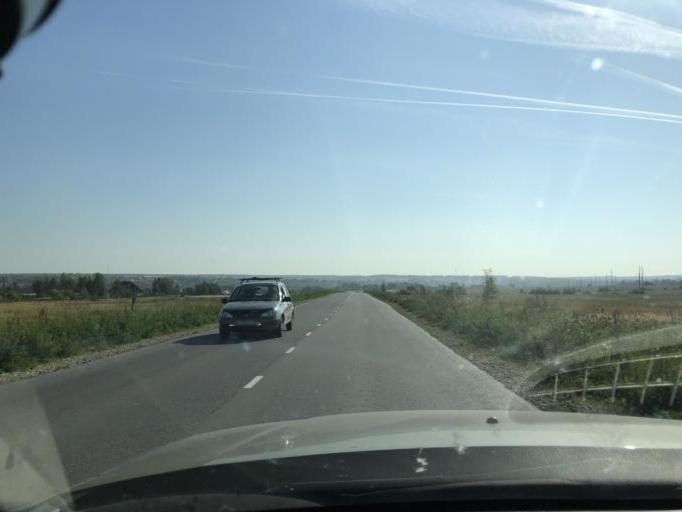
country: RU
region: Tula
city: Yasnogorsk
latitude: 54.4694
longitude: 37.6667
